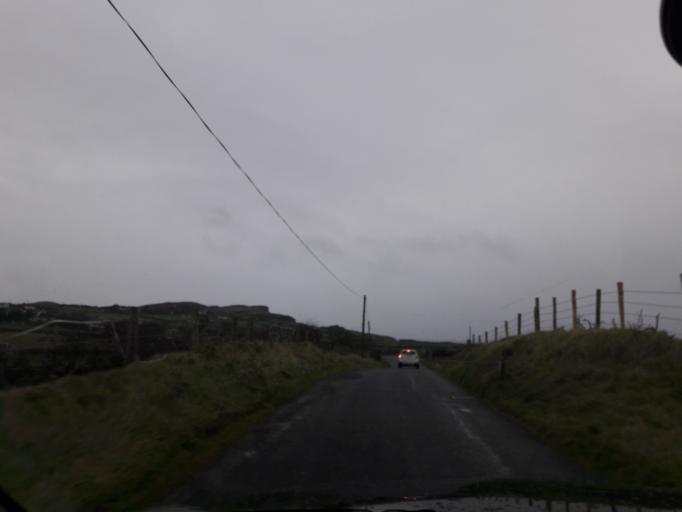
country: IE
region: Ulster
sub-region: County Donegal
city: Buncrana
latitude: 55.2466
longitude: -7.6222
